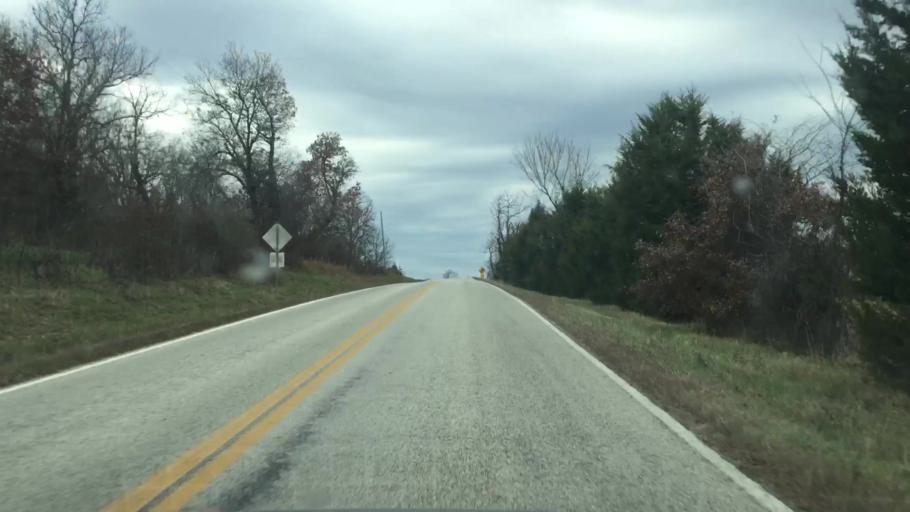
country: US
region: Missouri
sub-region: Saint Clair County
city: Osceola
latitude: 37.9890
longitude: -93.6170
